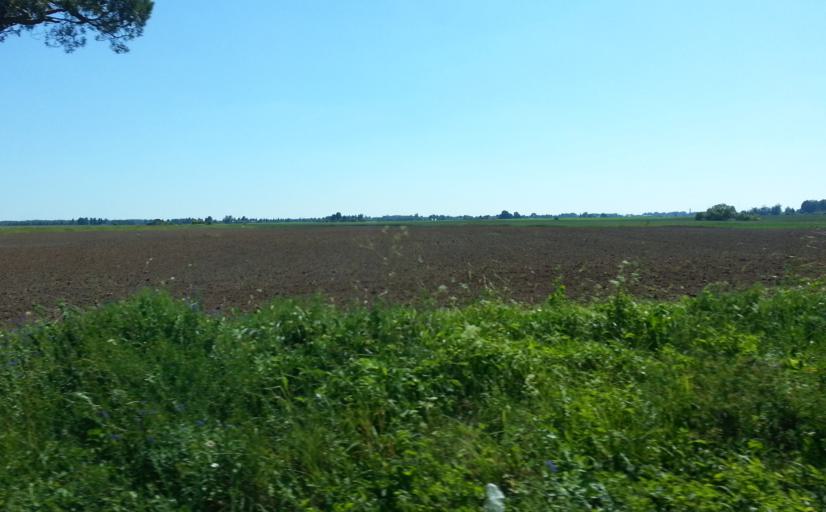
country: LT
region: Panevezys
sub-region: Birzai
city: Birzai
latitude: 56.2121
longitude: 24.6786
